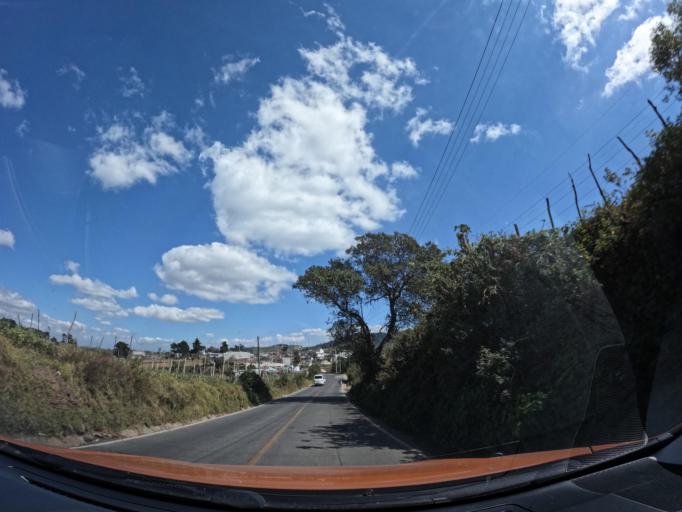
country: GT
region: Chimaltenango
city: Patzun
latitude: 14.6476
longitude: -91.0414
